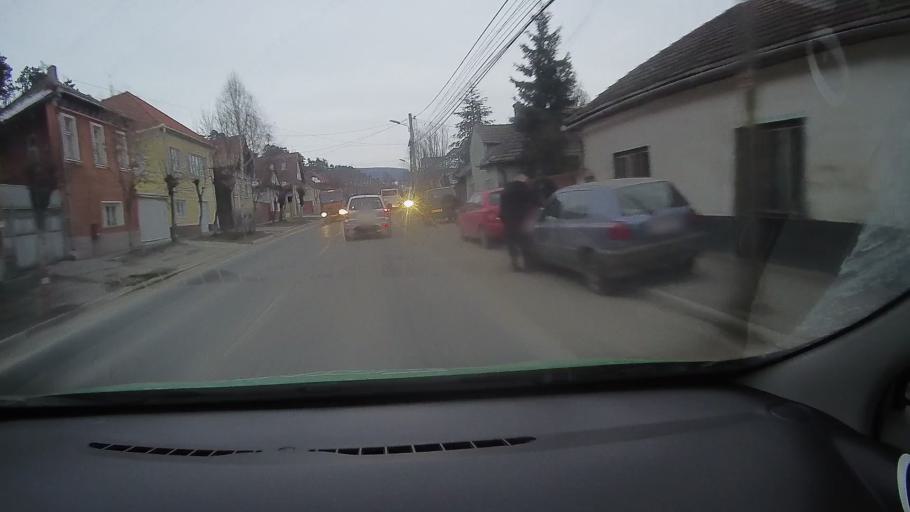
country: RO
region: Harghita
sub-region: Municipiul Odorheiu Secuiesc
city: Odorheiu Secuiesc
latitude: 46.2965
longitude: 25.2889
